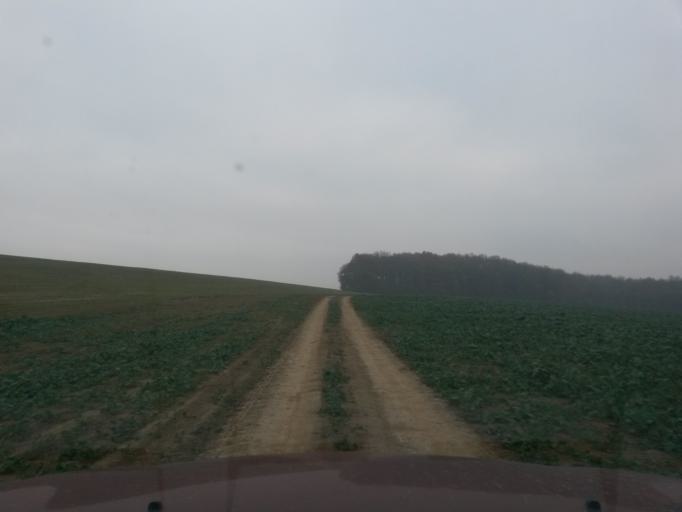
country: SK
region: Presovsky
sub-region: Okres Presov
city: Presov
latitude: 48.8850
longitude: 21.2808
